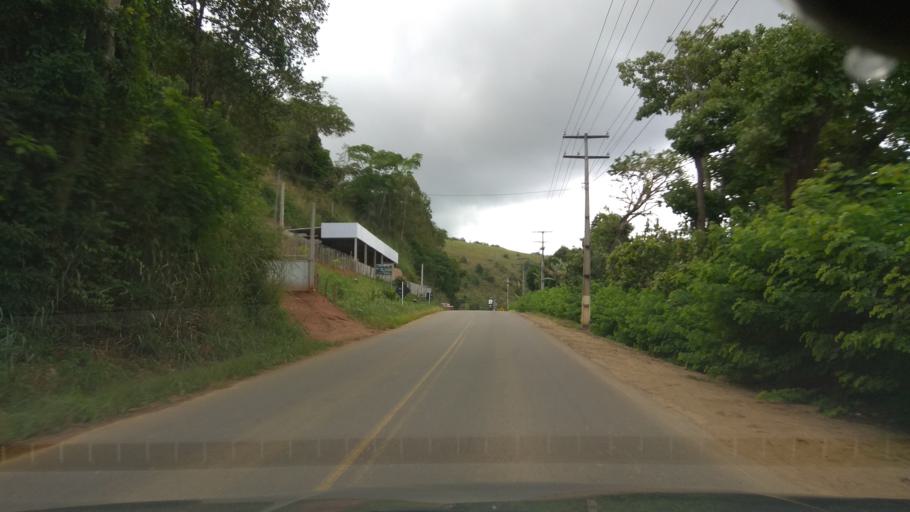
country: BR
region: Bahia
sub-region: Mutuipe
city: Mutuipe
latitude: -13.2517
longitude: -39.5665
